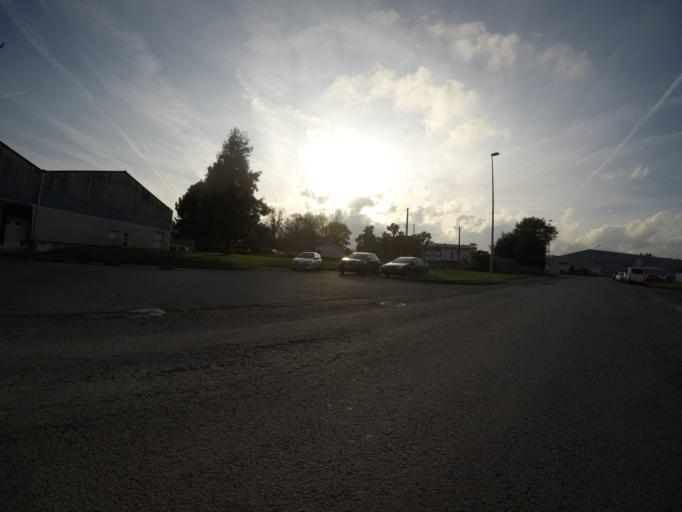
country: FR
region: Brittany
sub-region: Departement des Cotes-d'Armor
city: Guingamp
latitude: 48.5475
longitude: -3.1631
